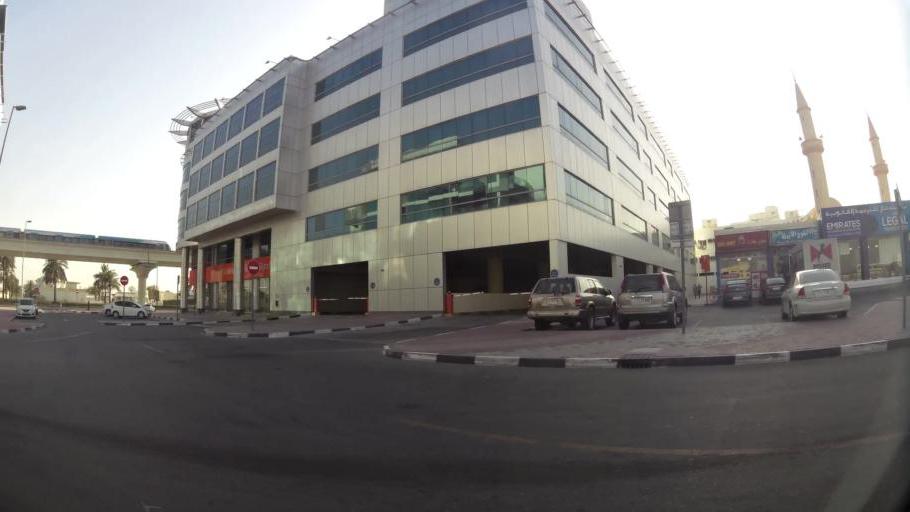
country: AE
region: Ash Shariqah
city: Sharjah
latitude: 25.2672
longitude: 55.3834
